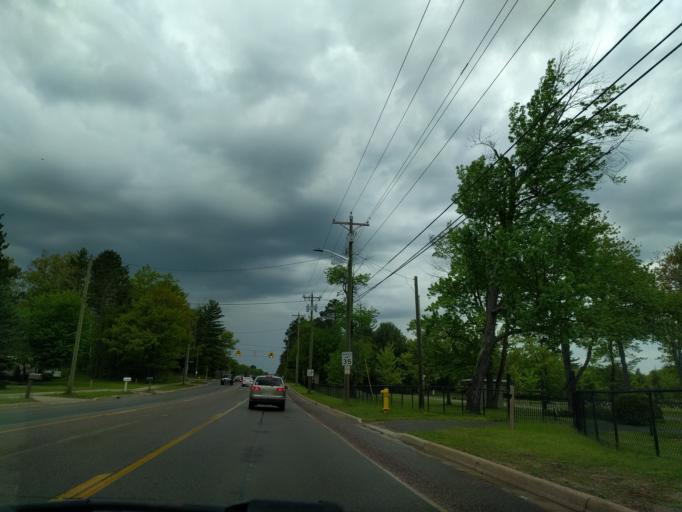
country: US
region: Michigan
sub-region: Marquette County
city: Trowbridge Park
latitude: 46.5641
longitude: -87.4186
